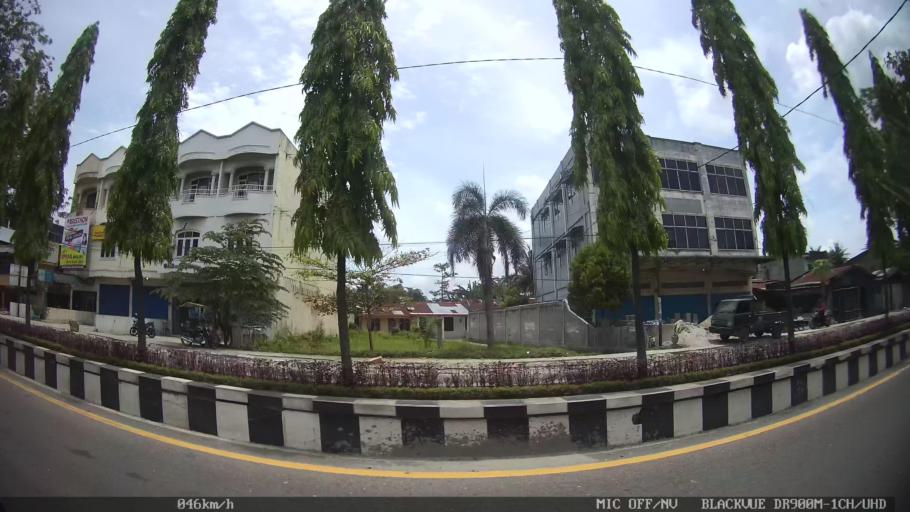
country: ID
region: North Sumatra
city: Percut
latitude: 3.5538
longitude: 98.8770
